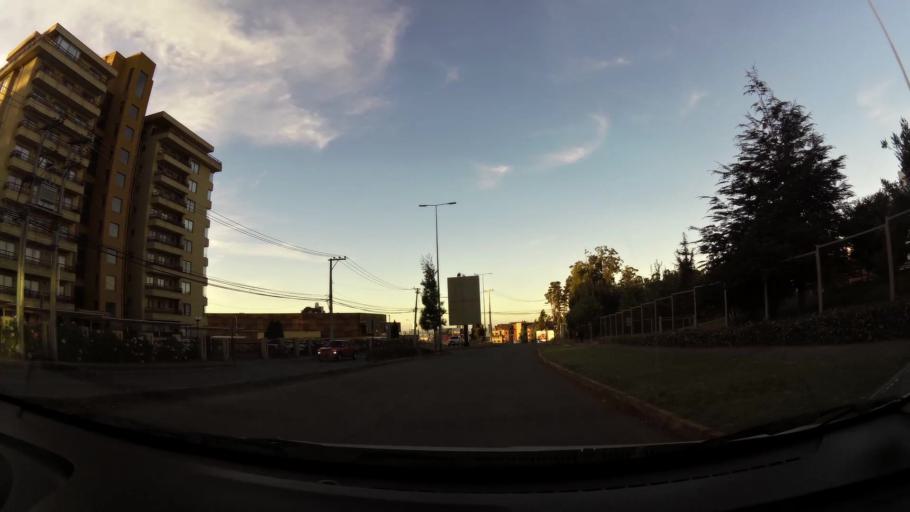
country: CL
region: Biobio
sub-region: Provincia de Concepcion
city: Concepcion
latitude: -36.8504
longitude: -73.0931
